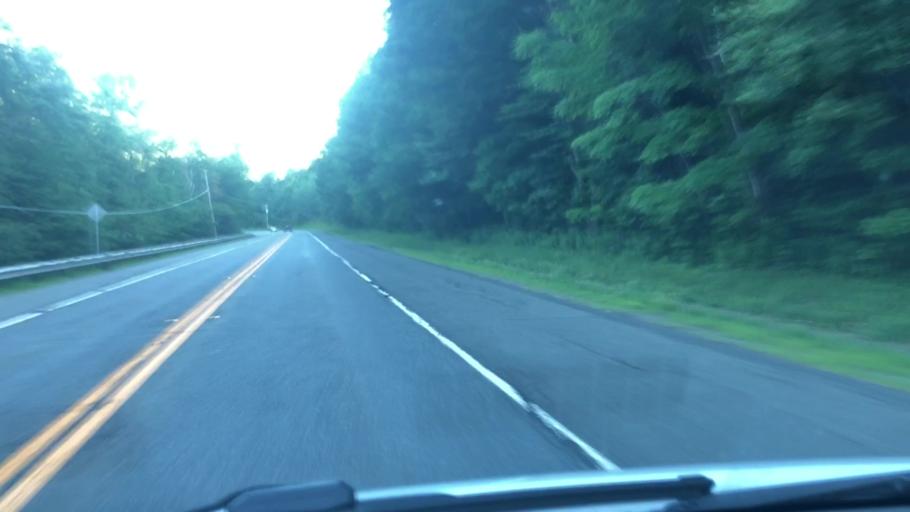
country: US
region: Massachusetts
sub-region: Berkshire County
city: Hinsdale
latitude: 42.4950
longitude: -73.0043
